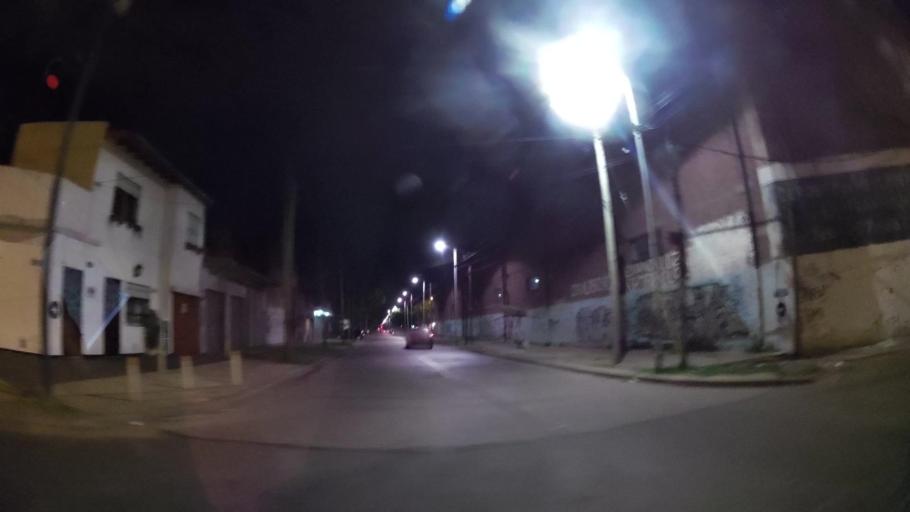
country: AR
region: Buenos Aires
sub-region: Partido de Lanus
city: Lanus
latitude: -34.7148
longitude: -58.3475
